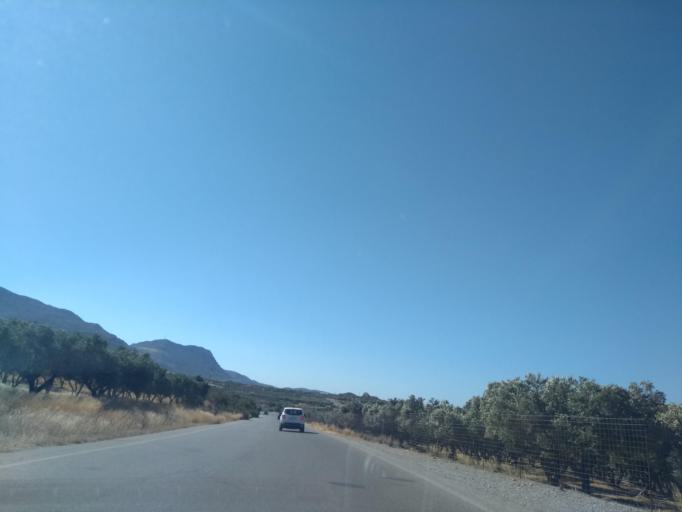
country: GR
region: Crete
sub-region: Nomos Chanias
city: Palaiochora
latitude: 35.2975
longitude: 23.5390
